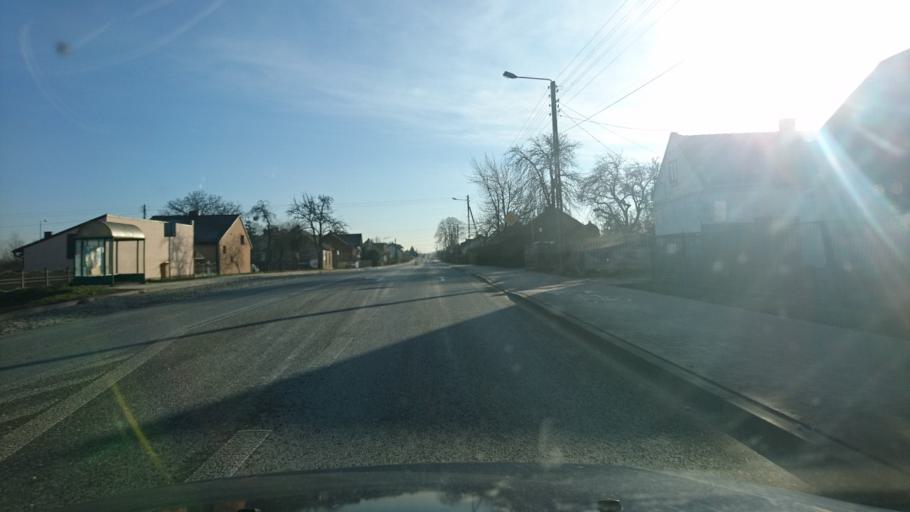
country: PL
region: Silesian Voivodeship
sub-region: Powiat klobucki
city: Starokrzepice
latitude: 51.0176
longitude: 18.6531
